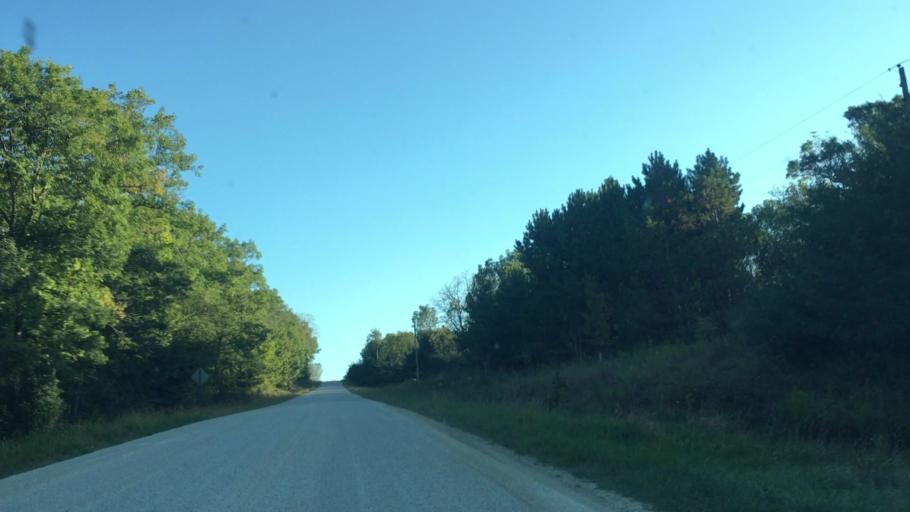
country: US
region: Minnesota
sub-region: Fillmore County
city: Preston
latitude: 43.7805
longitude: -92.0294
